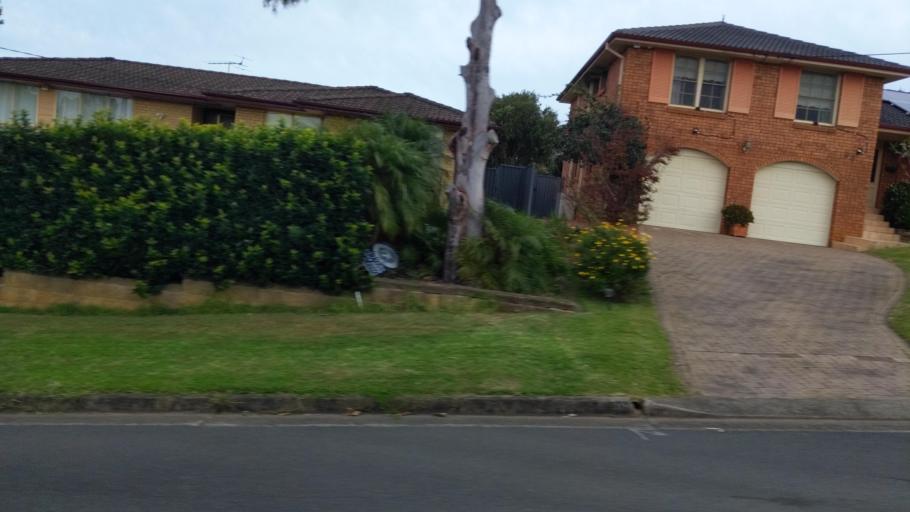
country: AU
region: New South Wales
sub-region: The Hills Shire
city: Baulkham Hills
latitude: -33.7489
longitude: 150.9637
